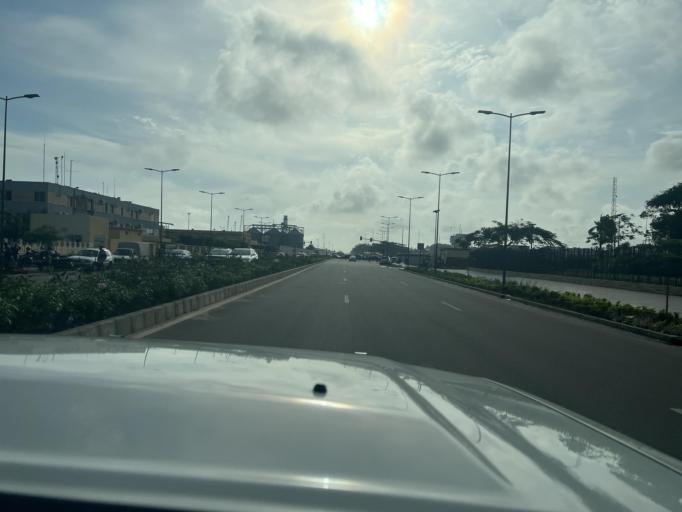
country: BJ
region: Littoral
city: Cotonou
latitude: 6.3513
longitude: 2.4296
